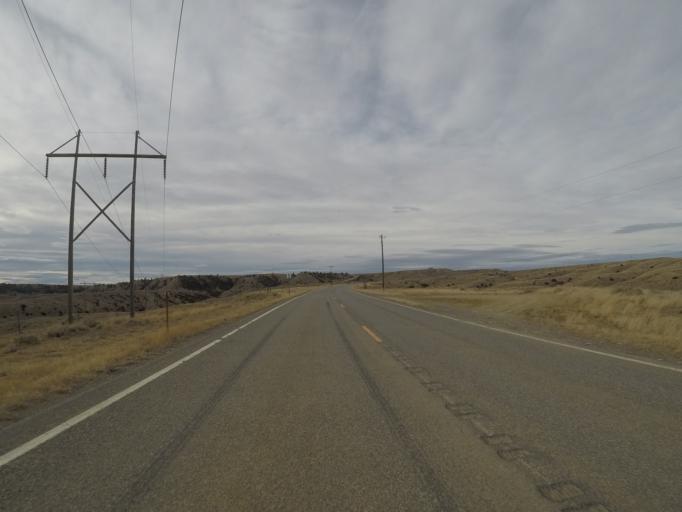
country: US
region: Montana
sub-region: Yellowstone County
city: Laurel
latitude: 45.8493
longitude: -108.7444
